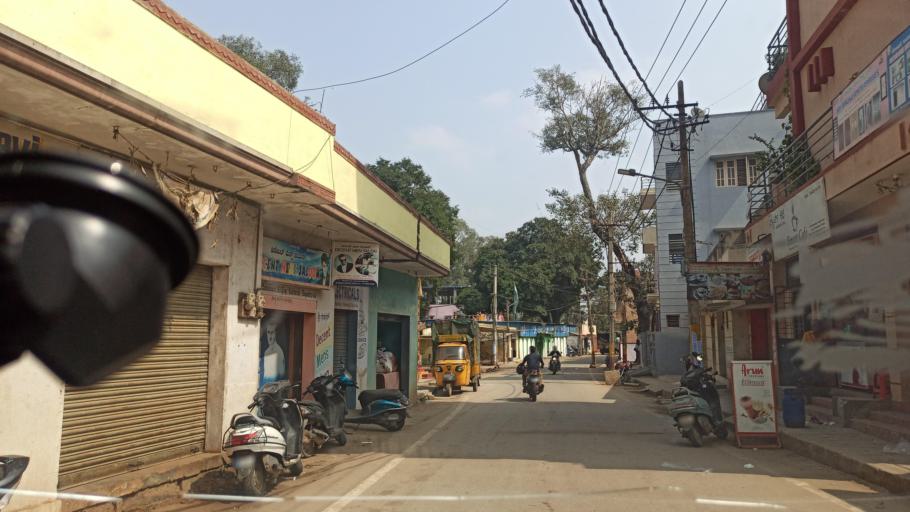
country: IN
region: Karnataka
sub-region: Bangalore Urban
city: Yelahanka
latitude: 13.1043
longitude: 77.5947
